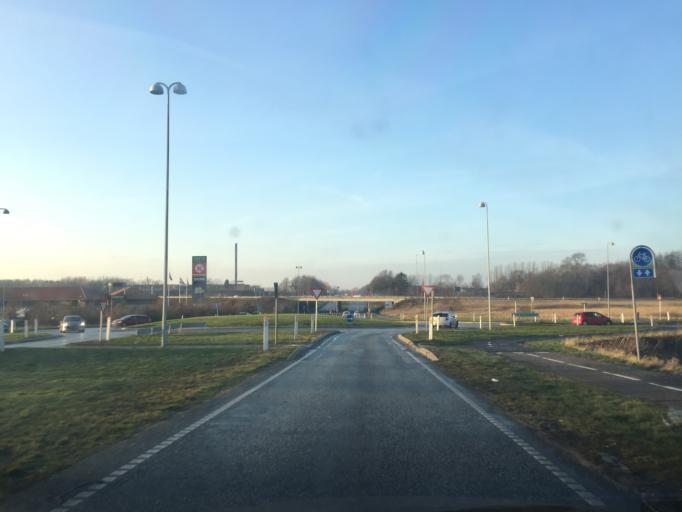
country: DK
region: Zealand
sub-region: Slagelse Kommune
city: Slagelse
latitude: 55.3879
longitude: 11.3647
